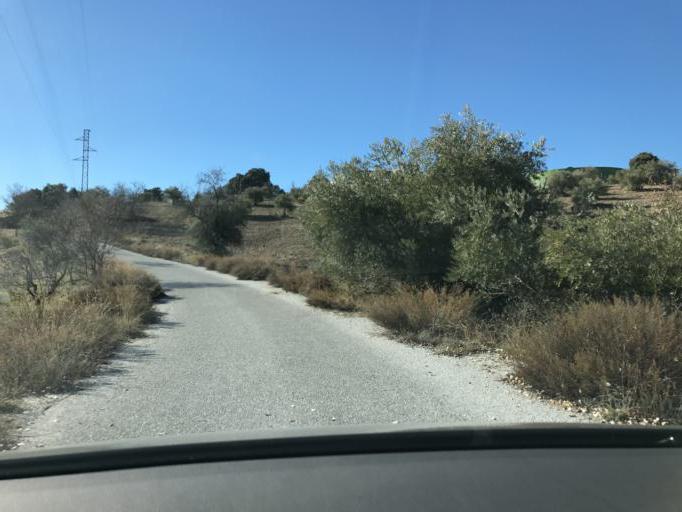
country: ES
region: Andalusia
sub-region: Provincia de Granada
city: Huetor Santillan
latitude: 37.2151
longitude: -3.5349
